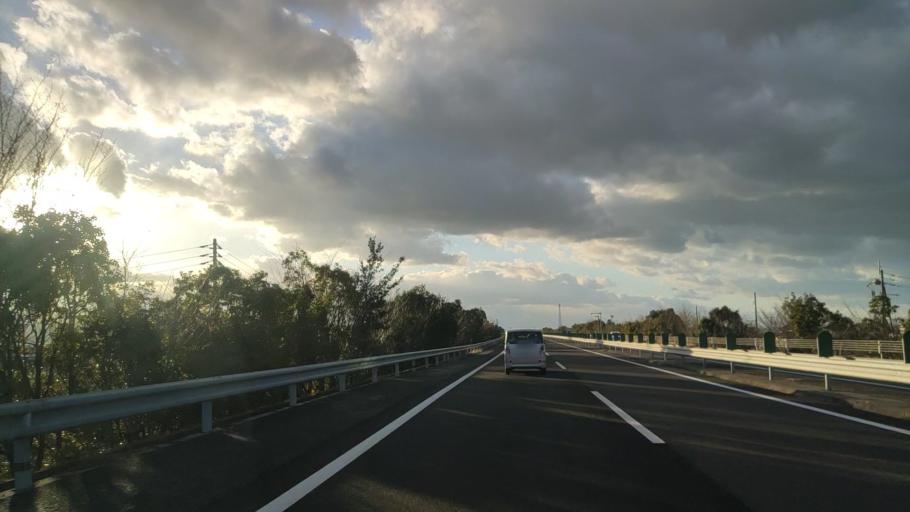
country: JP
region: Ehime
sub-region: Shikoku-chuo Shi
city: Matsuyama
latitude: 33.7859
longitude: 132.8687
